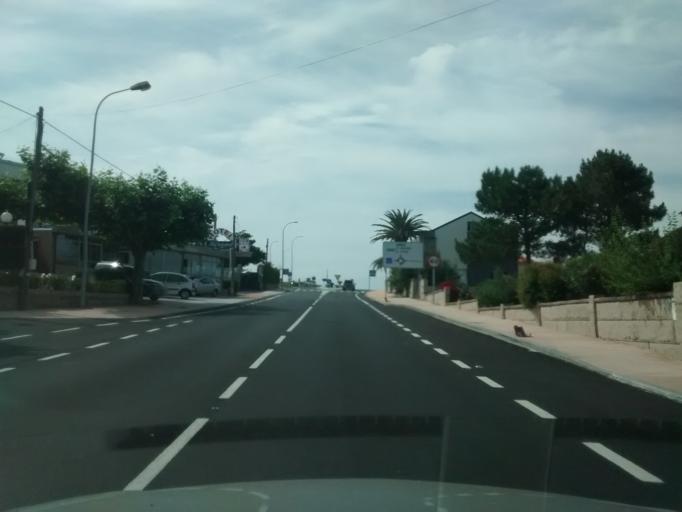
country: ES
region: Galicia
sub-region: Provincia de Pontevedra
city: Sanxenxo
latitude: 42.4211
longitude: -8.8729
